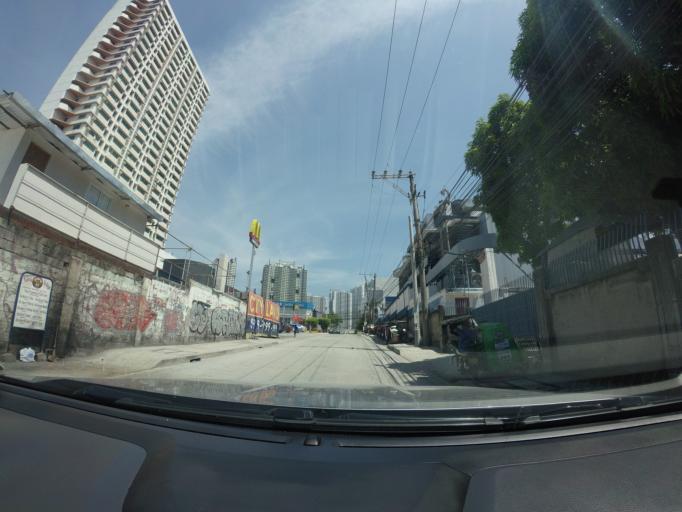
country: PH
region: Metro Manila
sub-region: Pasig
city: Pasig City
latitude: 14.5720
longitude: 121.0549
